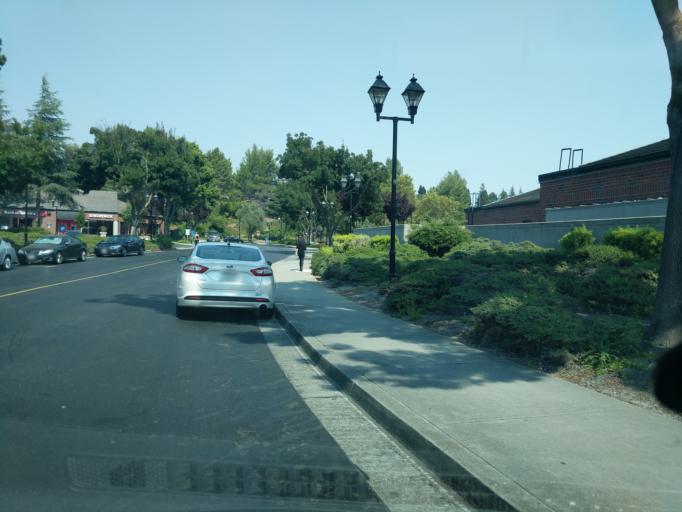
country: US
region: California
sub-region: Contra Costa County
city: San Ramon
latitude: 37.7644
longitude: -121.9524
